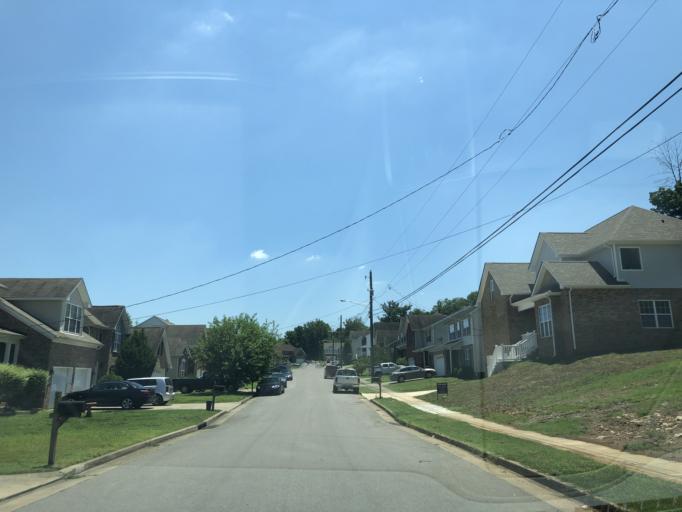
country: US
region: Tennessee
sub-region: Williamson County
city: Nolensville
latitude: 36.0199
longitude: -86.6543
